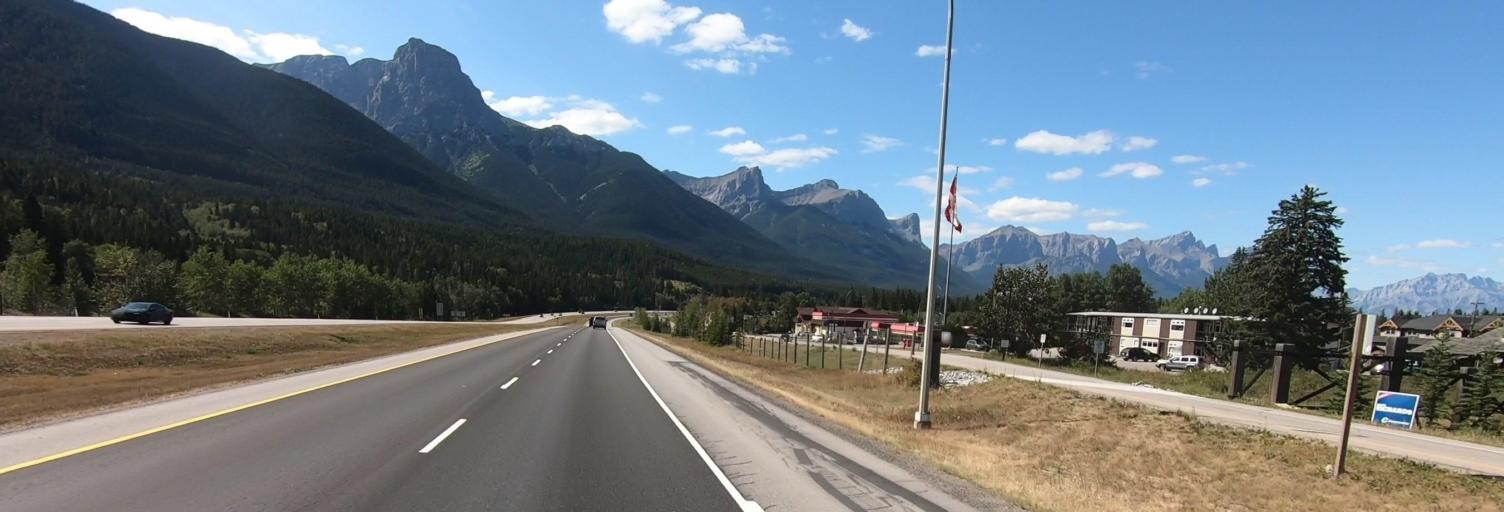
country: CA
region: Alberta
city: Canmore
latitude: 51.0391
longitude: -115.2614
